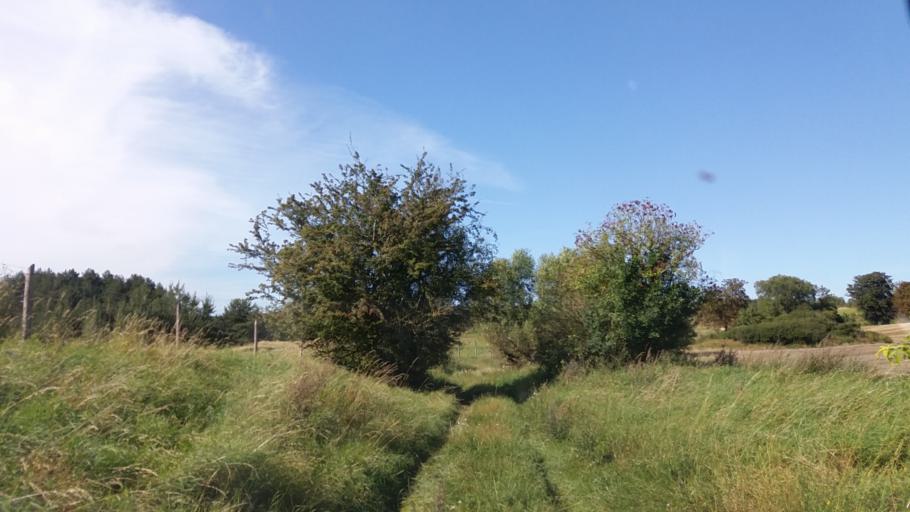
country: PL
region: West Pomeranian Voivodeship
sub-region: Powiat choszczenski
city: Krzecin
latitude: 53.1267
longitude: 15.5014
